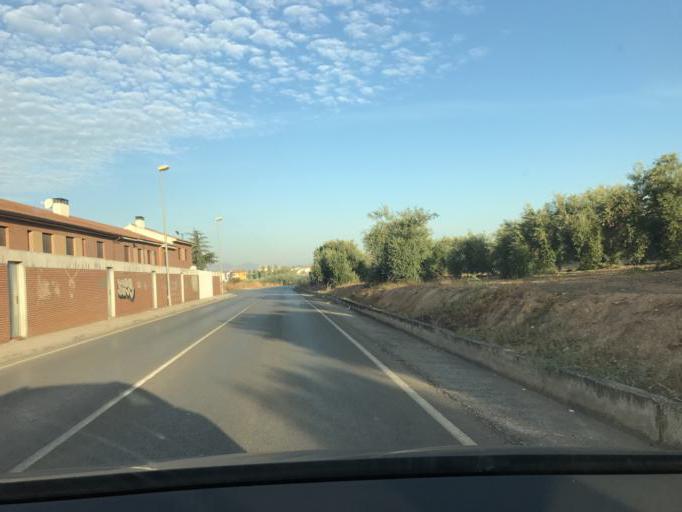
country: ES
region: Andalusia
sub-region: Provincia de Granada
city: Peligros
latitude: 37.2291
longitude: -3.6192
